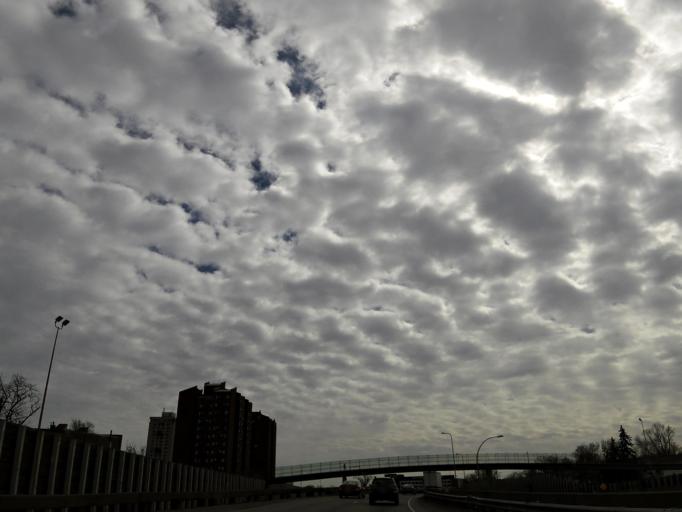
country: US
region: Minnesota
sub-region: Hennepin County
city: Minneapolis
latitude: 44.9603
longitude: -93.2694
